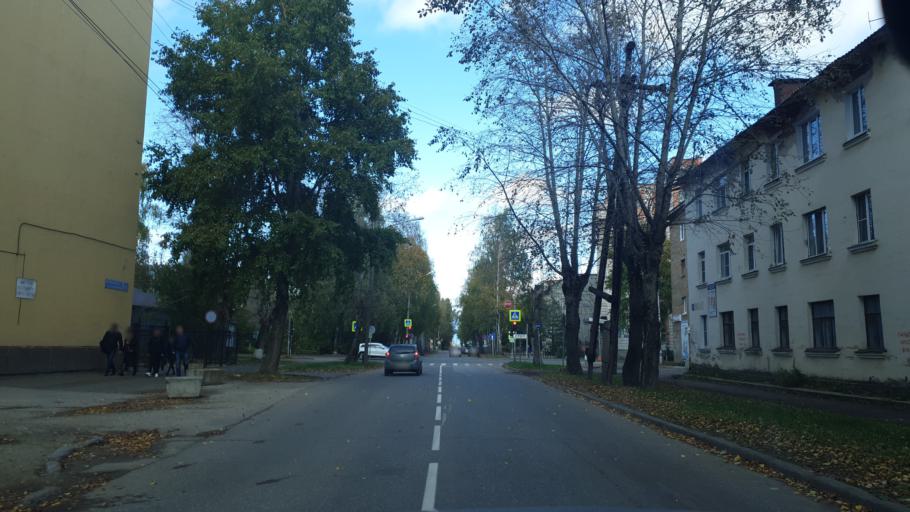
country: RU
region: Komi Republic
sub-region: Syktyvdinskiy Rayon
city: Syktyvkar
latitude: 61.6651
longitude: 50.8464
